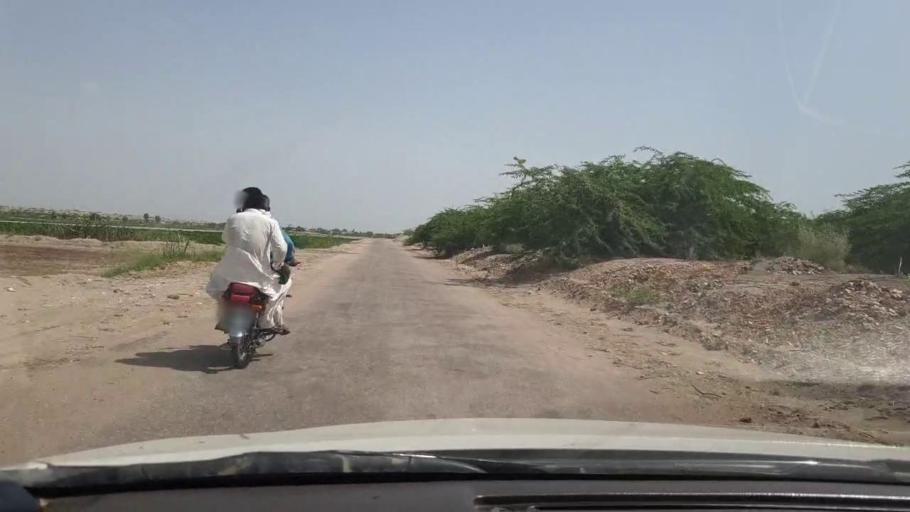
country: PK
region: Sindh
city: Rohri
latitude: 27.4876
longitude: 69.0539
